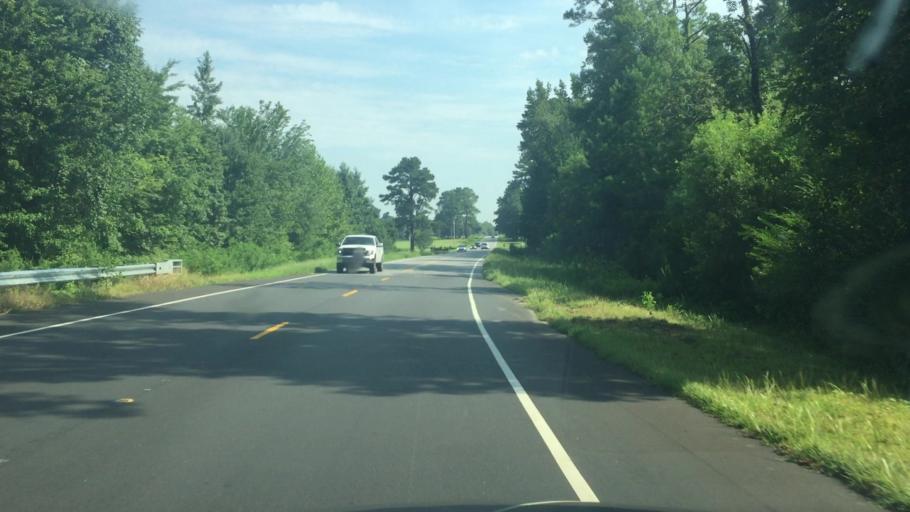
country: US
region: North Carolina
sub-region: Columbus County
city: Chadbourn
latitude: 34.2557
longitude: -78.8181
